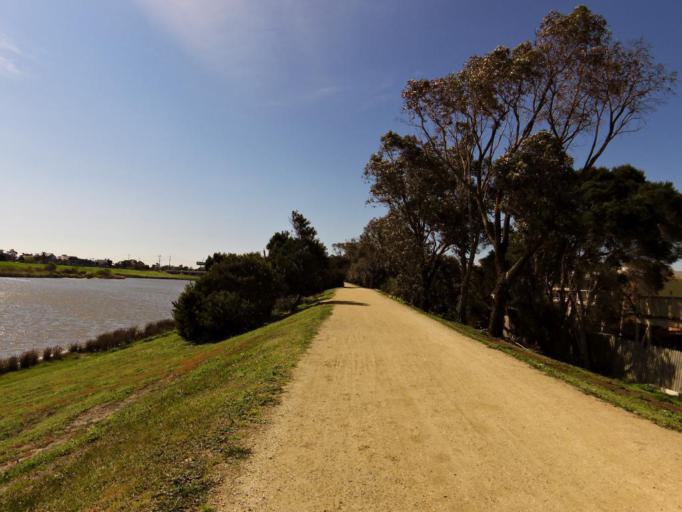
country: AU
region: Victoria
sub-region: Kingston
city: Patterson Lakes
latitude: -38.0625
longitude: 145.1441
